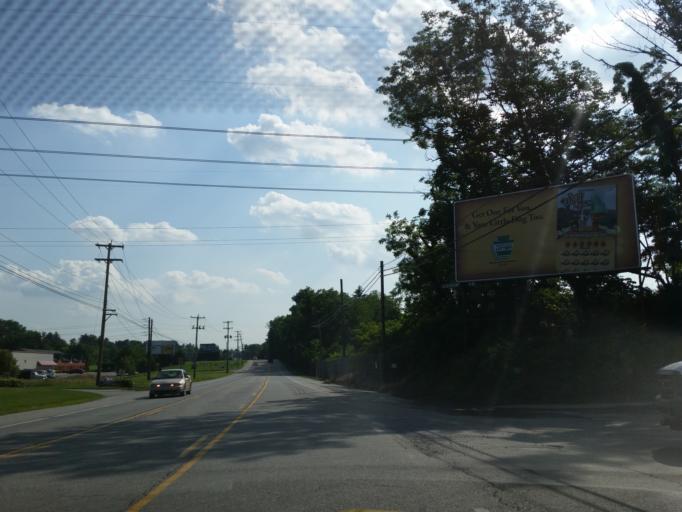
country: US
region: Pennsylvania
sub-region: York County
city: Yorklyn
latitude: 39.9989
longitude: -76.6256
